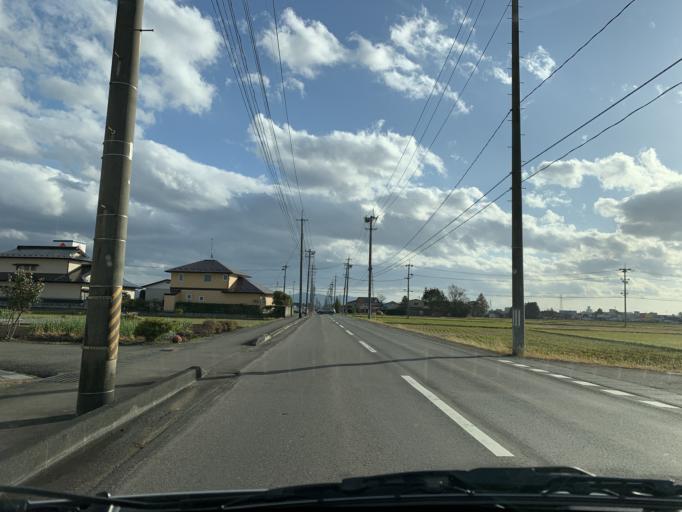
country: JP
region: Iwate
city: Mizusawa
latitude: 39.1587
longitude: 141.1577
